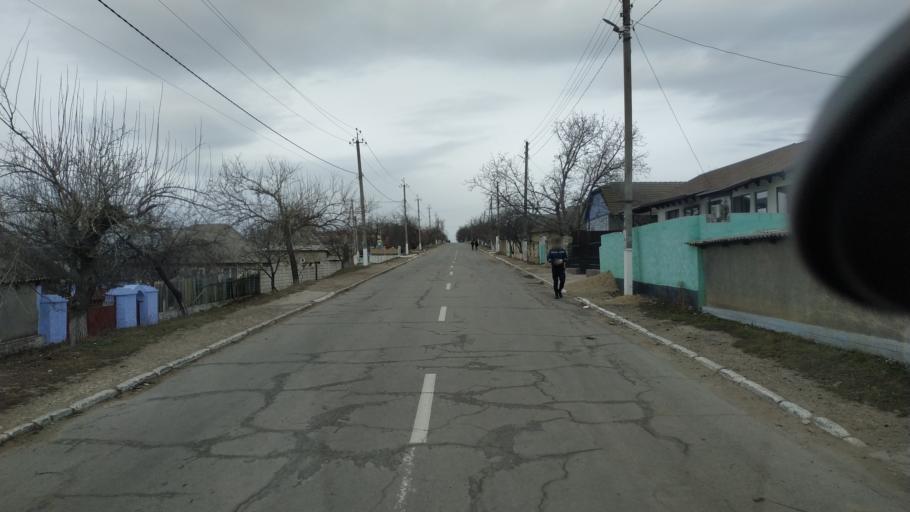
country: MD
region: Telenesti
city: Cocieri
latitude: 47.3494
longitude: 29.1173
